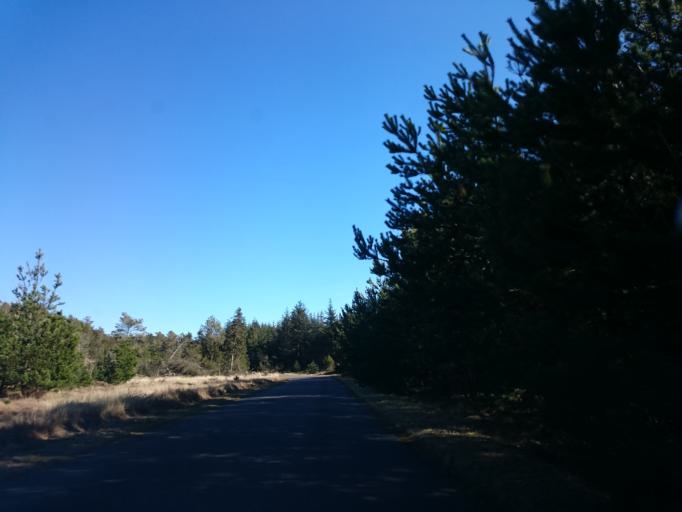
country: DK
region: North Denmark
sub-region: Hjorring Kommune
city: Sindal
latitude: 57.6172
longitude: 10.2926
